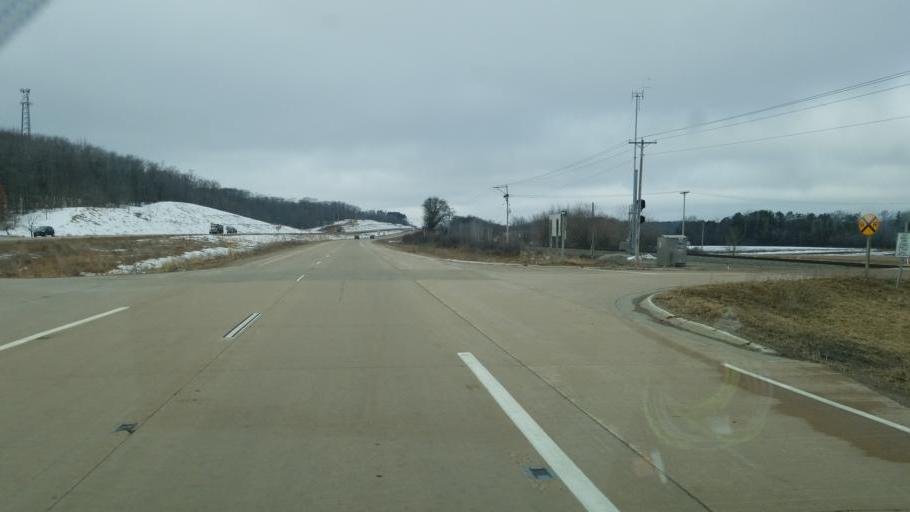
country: US
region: Wisconsin
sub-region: Portage County
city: Amherst
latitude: 44.4088
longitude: -89.2341
